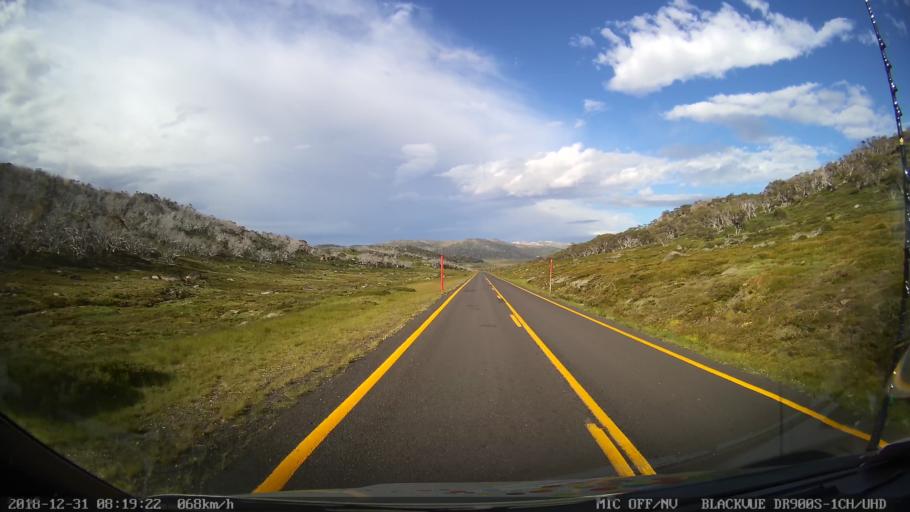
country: AU
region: New South Wales
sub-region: Snowy River
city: Jindabyne
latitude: -36.4189
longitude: 148.3866
